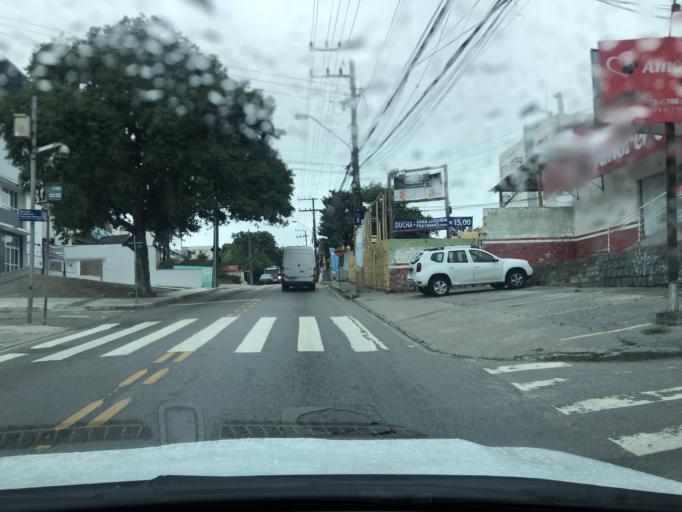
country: BR
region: Santa Catarina
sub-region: Florianopolis
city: Pantanal
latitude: -27.6099
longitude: -48.5231
